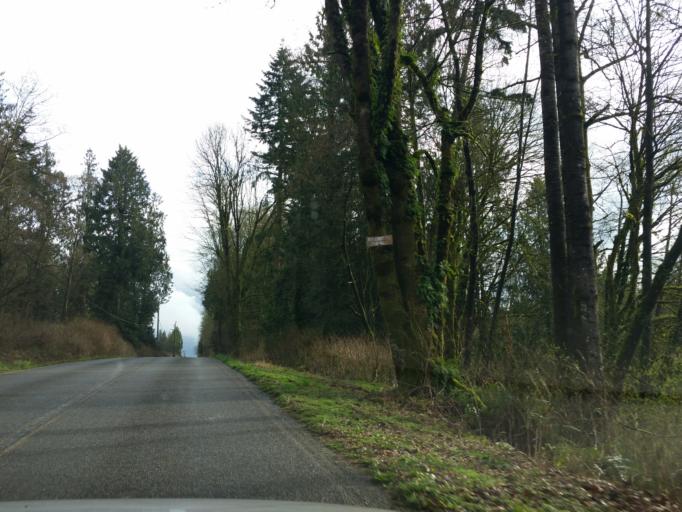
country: US
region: Washington
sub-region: Snohomish County
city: Cathcart
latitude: 47.8255
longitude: -122.0519
